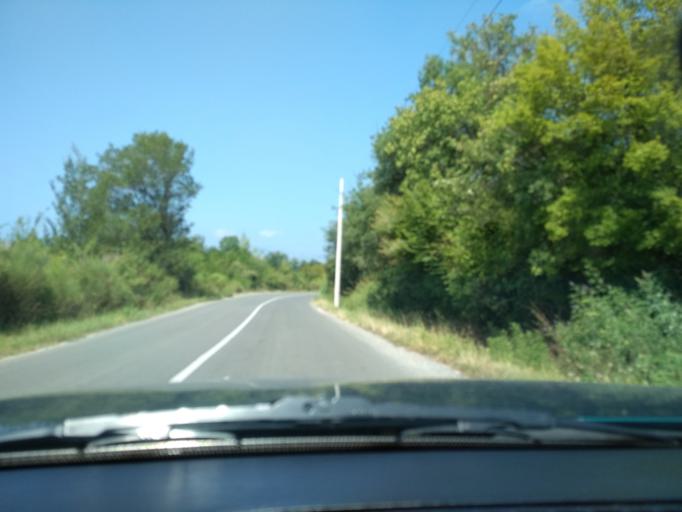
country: ME
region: Kotor
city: Kotor
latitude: 42.3919
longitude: 18.7567
